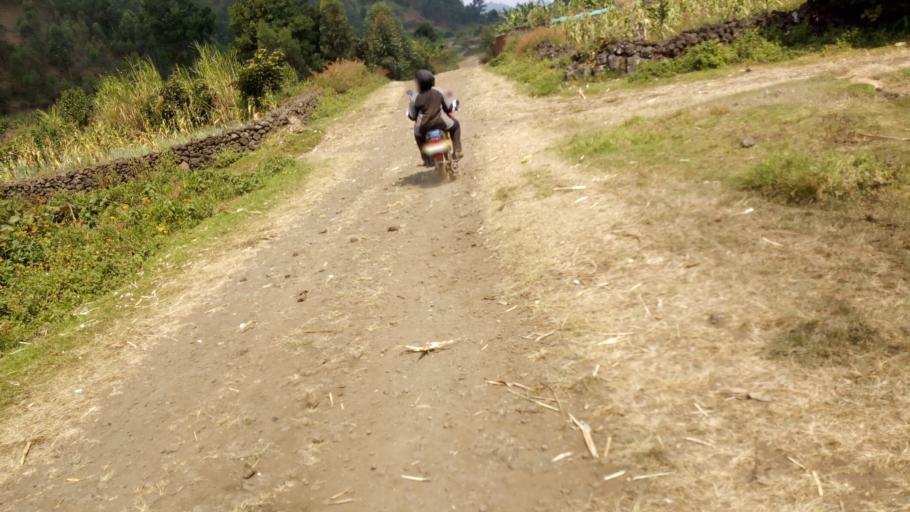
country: UG
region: Western Region
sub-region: Kisoro District
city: Kisoro
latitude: -1.3361
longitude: 29.7633
